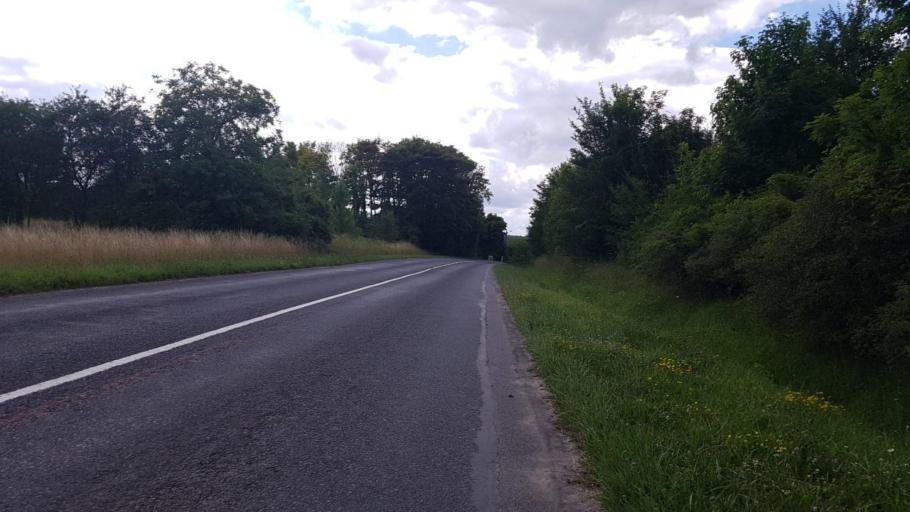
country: FR
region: Picardie
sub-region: Departement de l'Aisne
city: Crezancy
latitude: 49.0738
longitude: 3.5168
